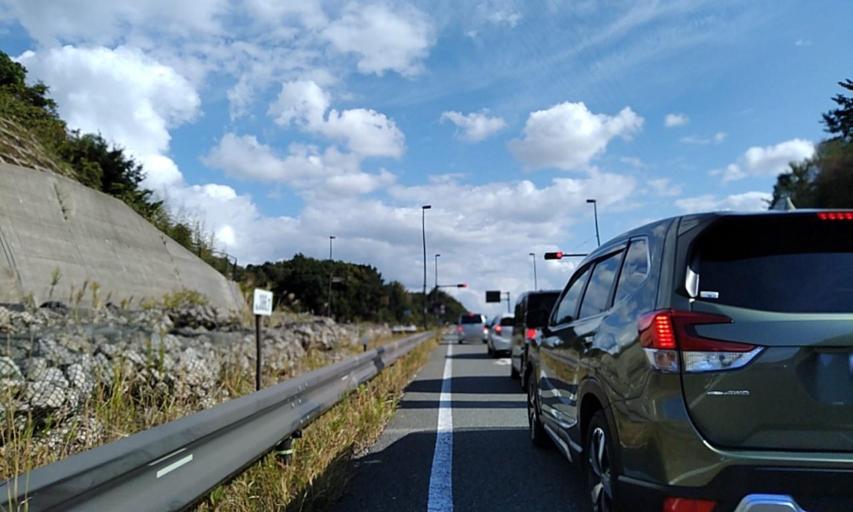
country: JP
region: Wakayama
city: Tanabe
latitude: 33.7495
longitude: 135.3602
